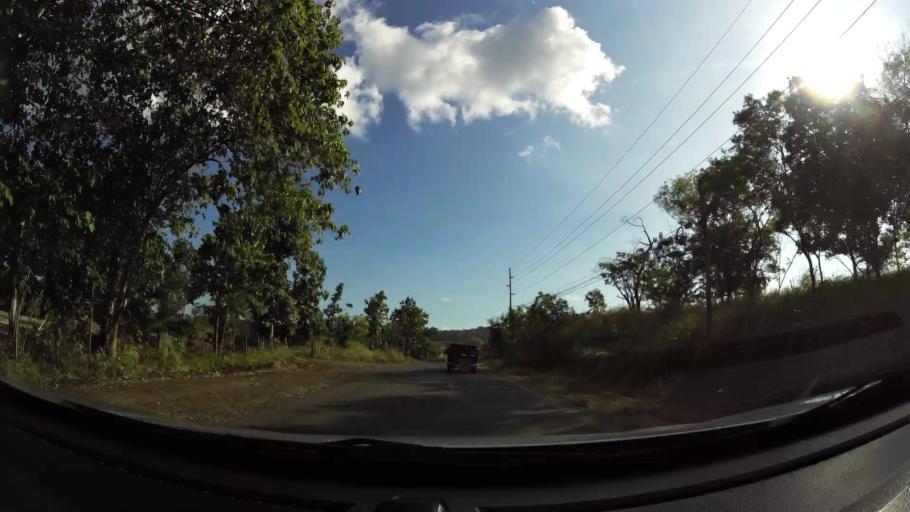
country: CR
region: Guanacaste
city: Sardinal
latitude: 10.5445
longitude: -85.6780
